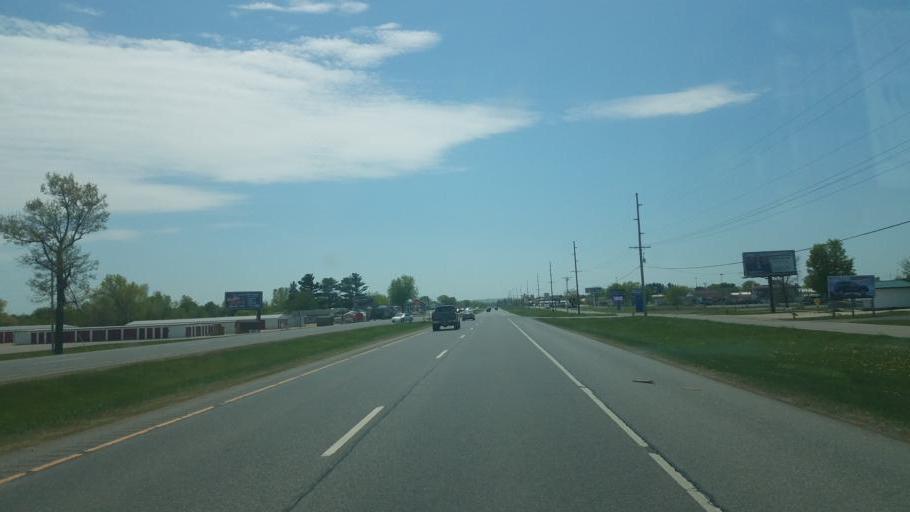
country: US
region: Wisconsin
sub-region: Monroe County
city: Tomah
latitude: 44.0094
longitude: -90.5052
